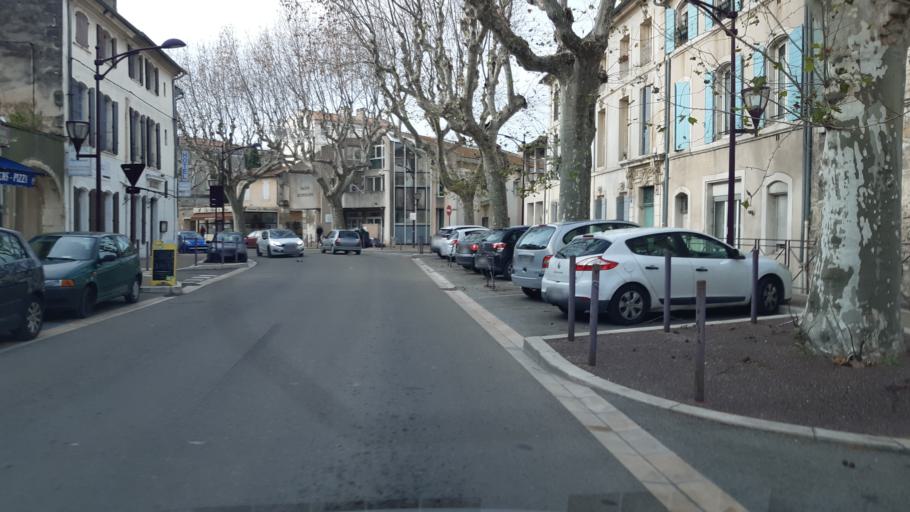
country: FR
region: Provence-Alpes-Cote d'Azur
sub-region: Departement des Bouches-du-Rhone
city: Tarascon
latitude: 43.8032
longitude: 4.6595
